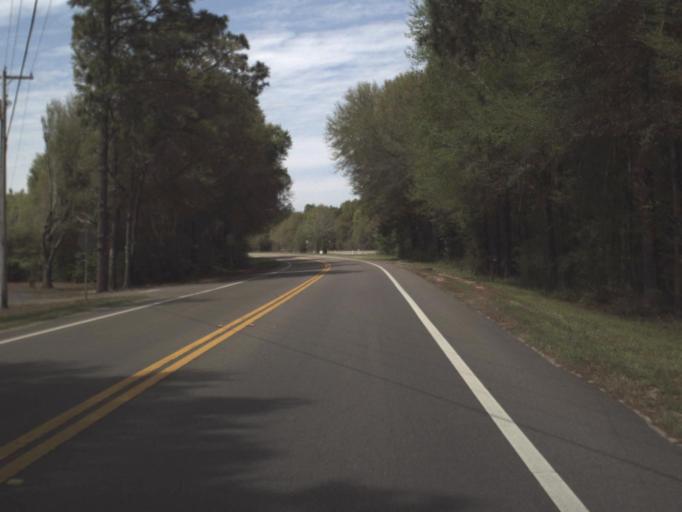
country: US
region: Florida
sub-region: Okaloosa County
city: Crestview
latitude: 30.7121
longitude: -86.7563
